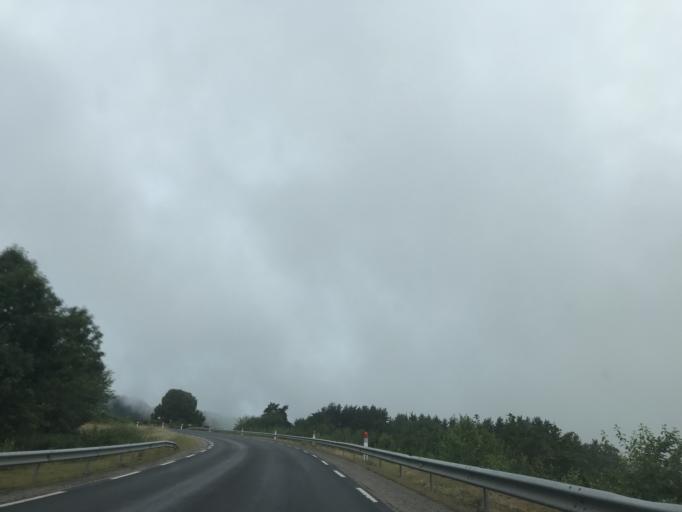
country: FR
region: Auvergne
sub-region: Departement de la Haute-Loire
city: Fontannes
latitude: 45.3486
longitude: 3.7310
